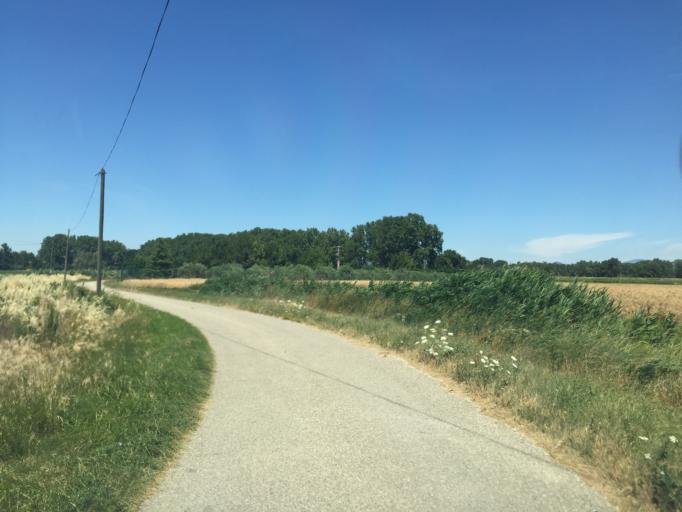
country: FR
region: Provence-Alpes-Cote d'Azur
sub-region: Departement du Vaucluse
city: Bedarrides
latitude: 44.0441
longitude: 4.9230
